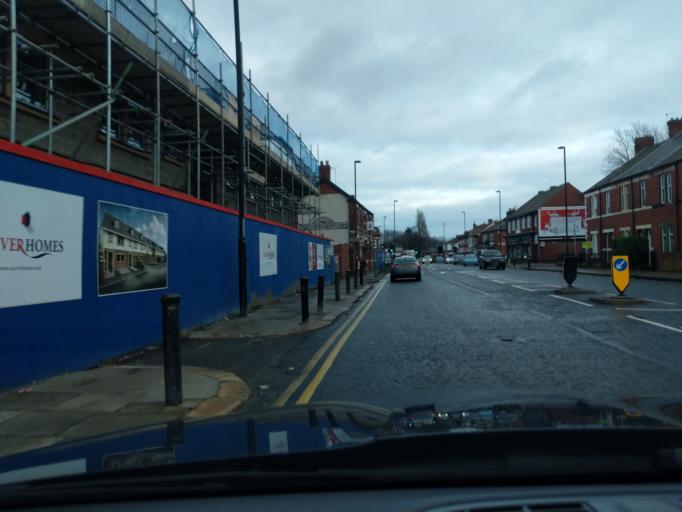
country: GB
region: England
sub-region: Borough of North Tyneside
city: Wallsend
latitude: 54.9844
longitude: -1.5604
